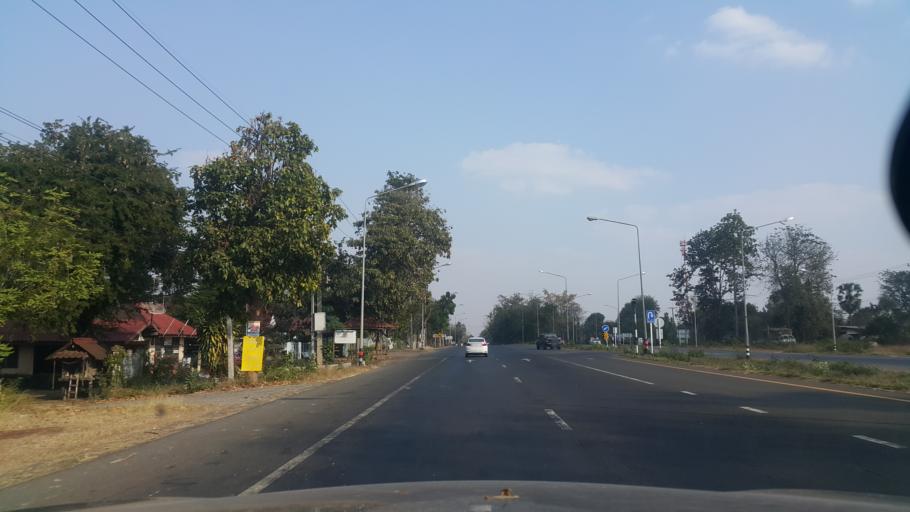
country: TH
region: Buriram
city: Non Suwan
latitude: 14.6484
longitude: 102.6659
